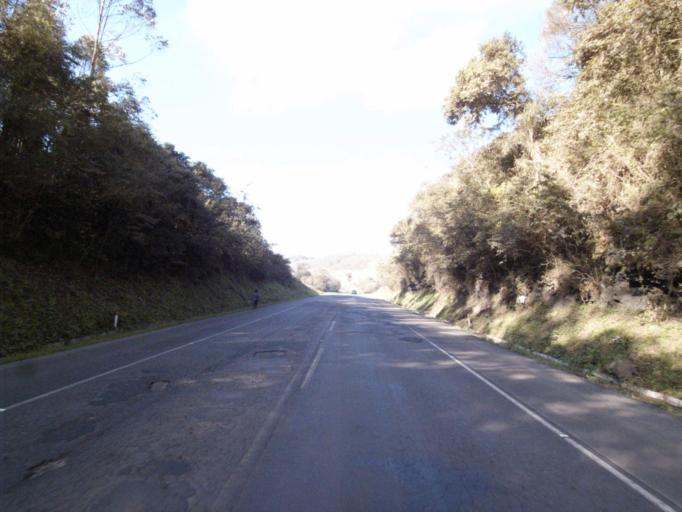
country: BR
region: Rio Grande do Sul
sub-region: Frederico Westphalen
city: Frederico Westphalen
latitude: -27.0512
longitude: -53.2293
